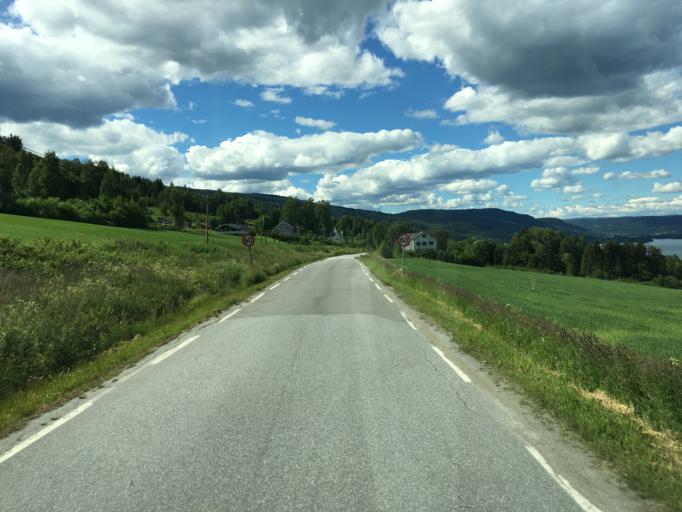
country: NO
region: Oppland
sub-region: Sondre Land
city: Hov
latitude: 60.7006
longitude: 10.2790
